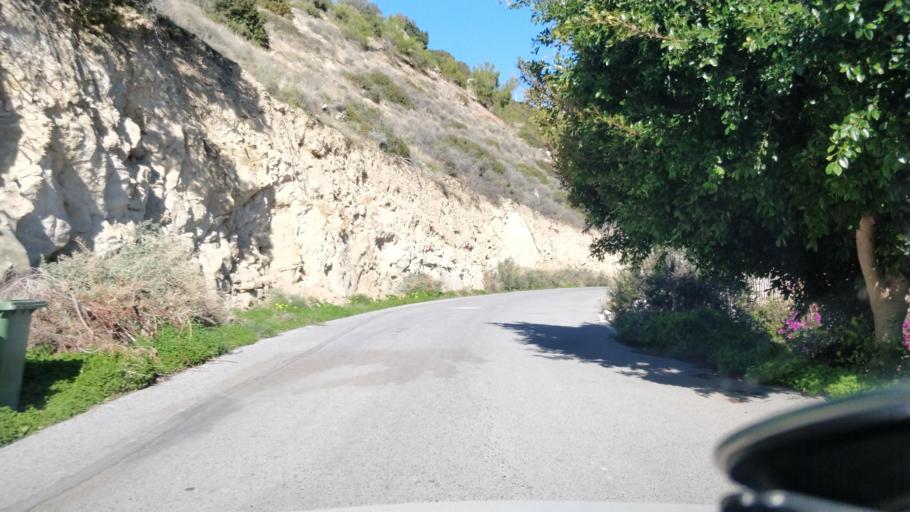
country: GR
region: Crete
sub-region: Nomos Lasithiou
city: Gra Liyia
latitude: 34.9879
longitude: 25.4812
